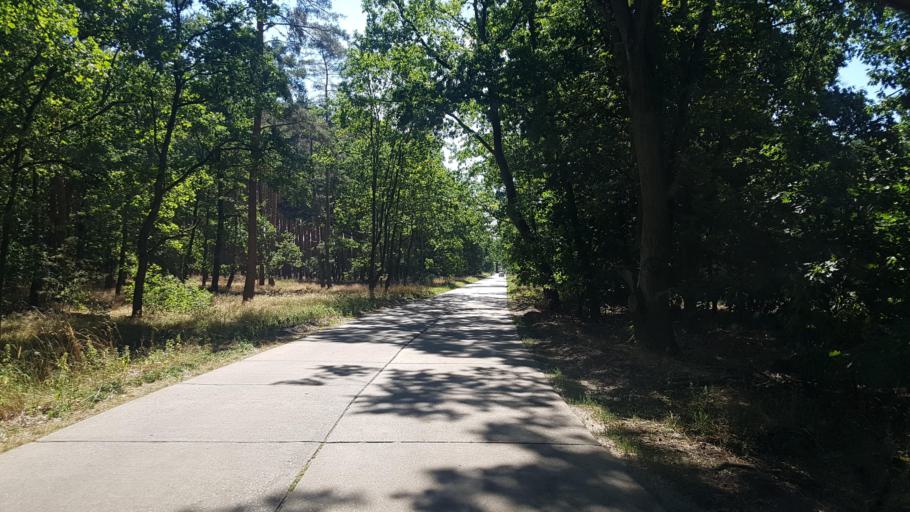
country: DE
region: Brandenburg
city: Golzow
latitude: 52.2993
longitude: 12.5817
